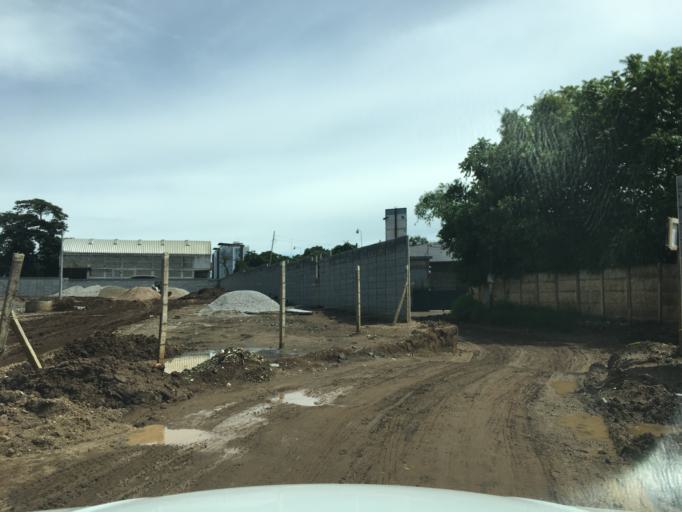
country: GT
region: Guatemala
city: Mixco
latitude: 14.6542
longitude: -90.5637
